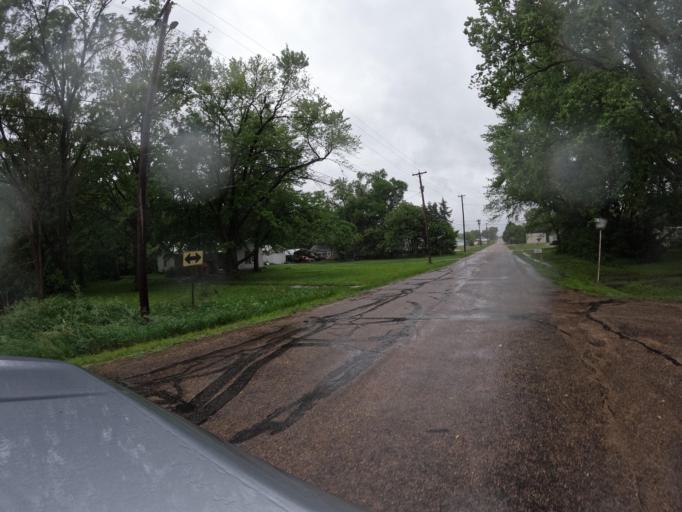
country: US
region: Nebraska
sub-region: Gage County
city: Wymore
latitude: 40.1234
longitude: -96.6574
